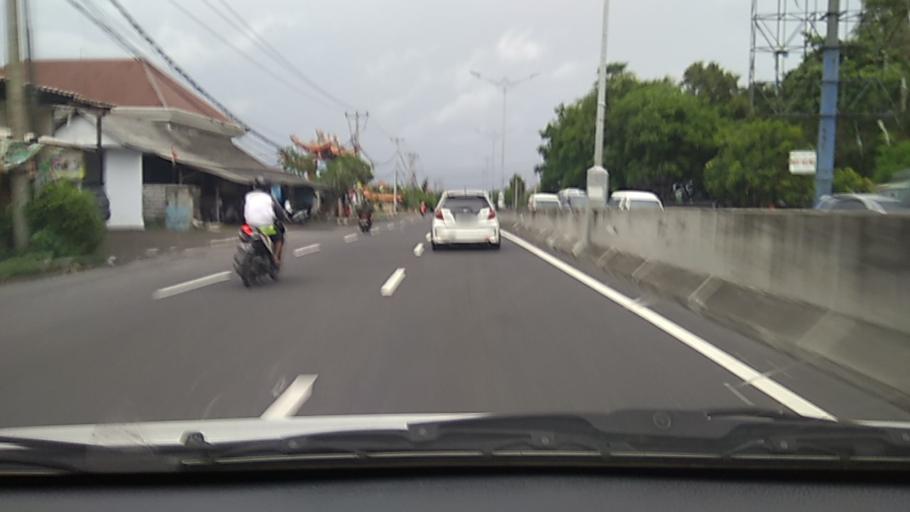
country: ID
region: Bali
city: Karyadharma
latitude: -8.7219
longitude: 115.2145
